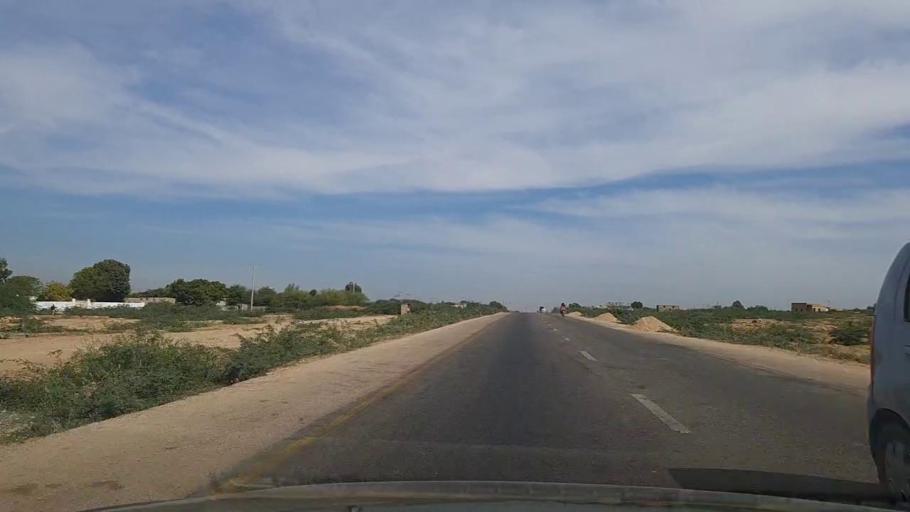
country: PK
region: Sindh
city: Thatta
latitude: 24.8334
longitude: 67.9982
